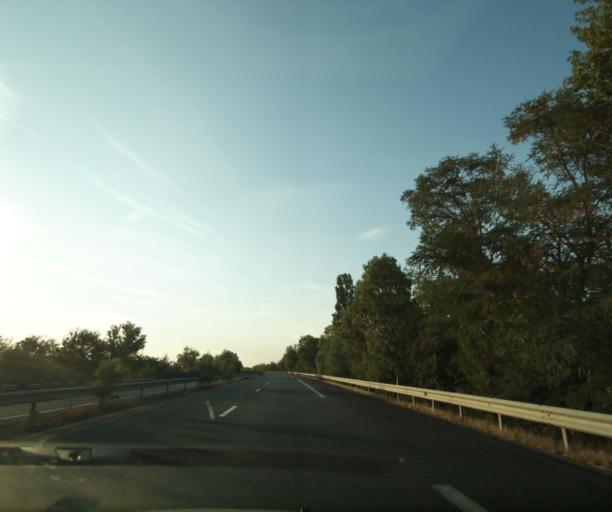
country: FR
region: Aquitaine
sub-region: Departement du Lot-et-Garonne
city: Layrac
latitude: 44.1386
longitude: 0.6702
